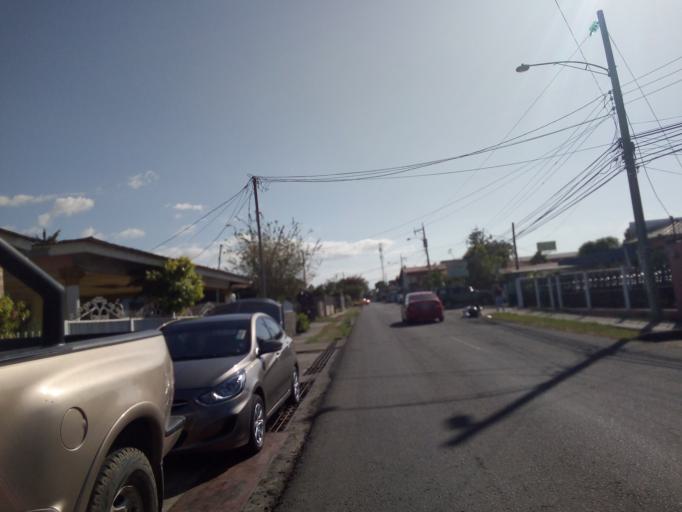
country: PA
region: Veraguas
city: Santiago de Veraguas
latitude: 8.1057
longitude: -80.9722
